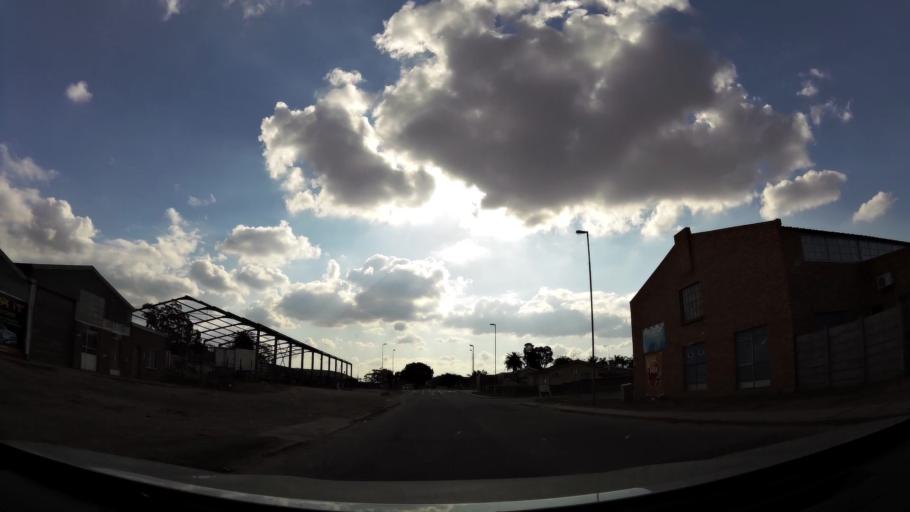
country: ZA
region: Eastern Cape
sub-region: Nelson Mandela Bay Metropolitan Municipality
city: Uitenhage
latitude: -33.7696
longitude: 25.3903
